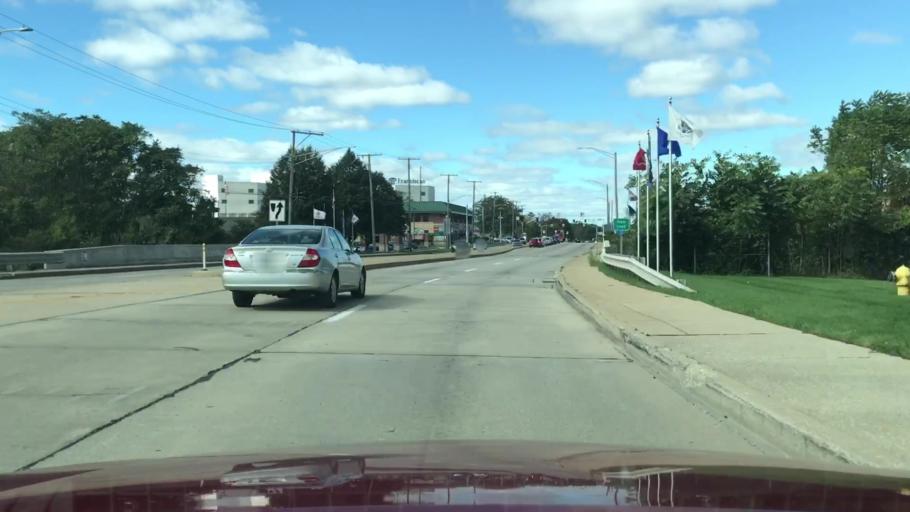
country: US
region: Indiana
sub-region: Lake County
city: Dyer
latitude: 41.4937
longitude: -87.5189
